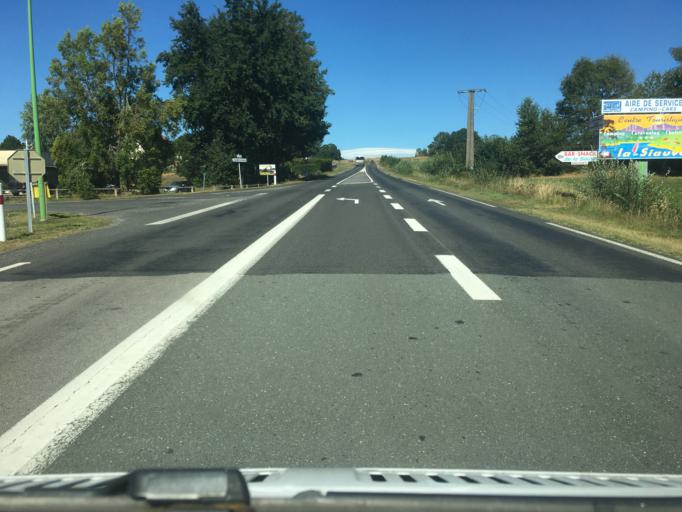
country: FR
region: Limousin
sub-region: Departement de la Correze
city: Bort-les-Orgues
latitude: 45.4258
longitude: 2.5063
